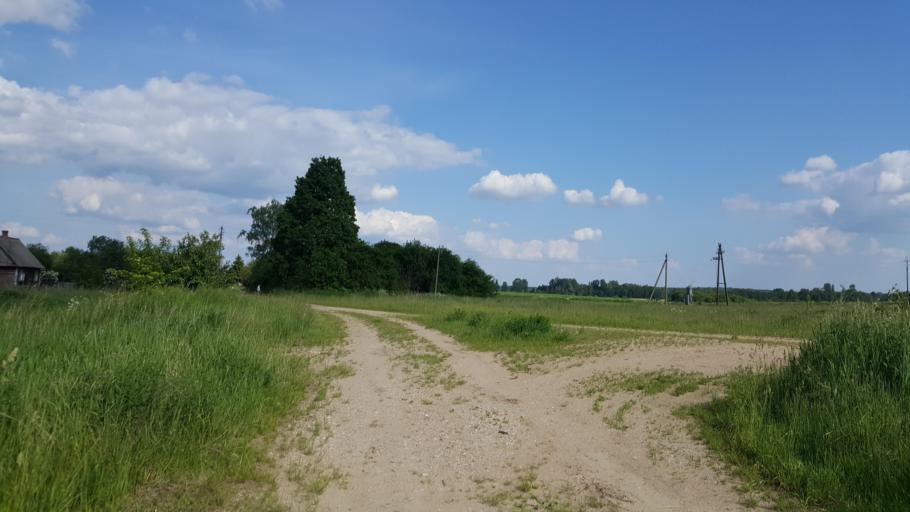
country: BY
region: Brest
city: Kamyanyets
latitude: 52.4189
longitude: 23.6603
